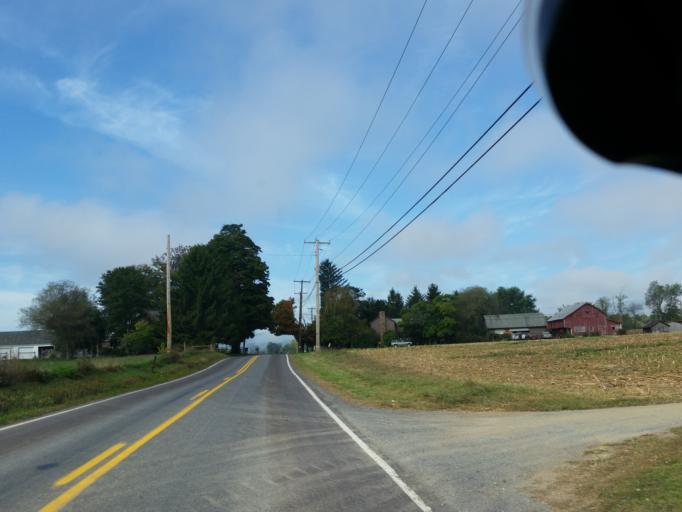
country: US
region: Pennsylvania
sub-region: Northumberland County
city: Dewart
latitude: 41.1226
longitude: -76.9847
